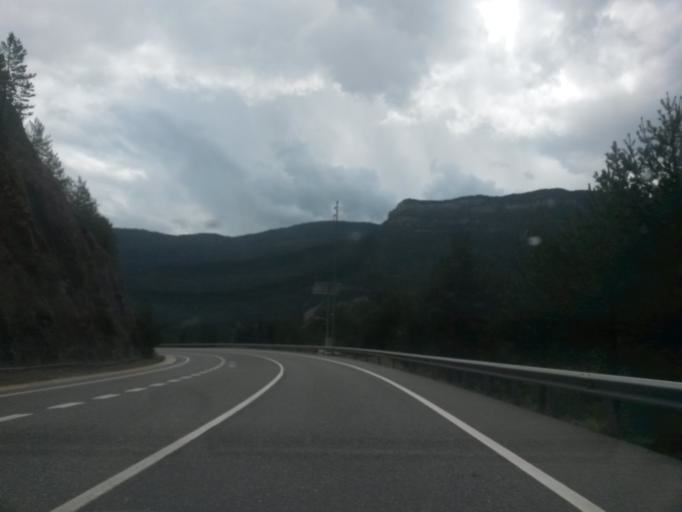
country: ES
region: Catalonia
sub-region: Provincia de Barcelona
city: Baga
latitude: 42.2667
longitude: 1.8523
